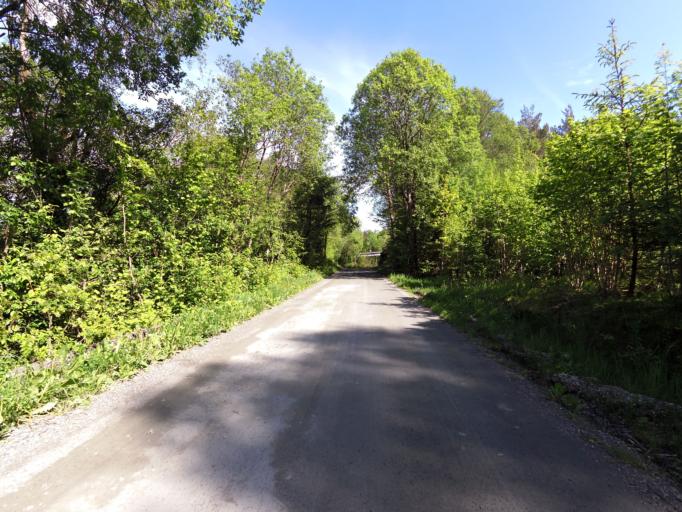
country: NO
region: Hordaland
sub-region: Stord
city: Leirvik
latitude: 59.7883
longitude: 5.4881
